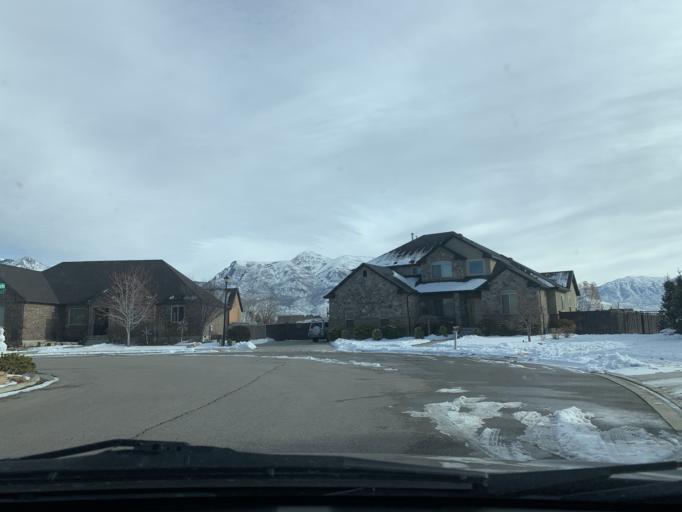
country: US
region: Utah
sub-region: Utah County
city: Lehi
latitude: 40.4104
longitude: -111.8229
